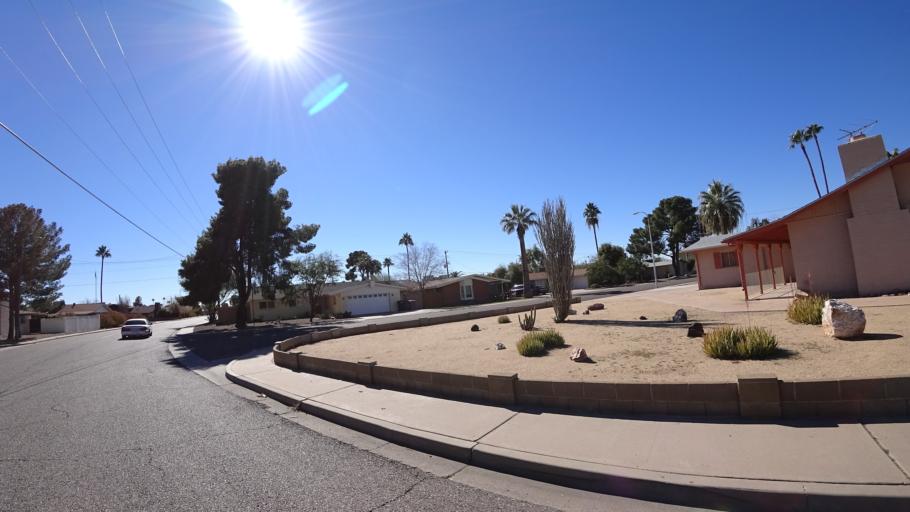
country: US
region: Arizona
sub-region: Maricopa County
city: Scottsdale
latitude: 33.5205
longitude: -111.8961
